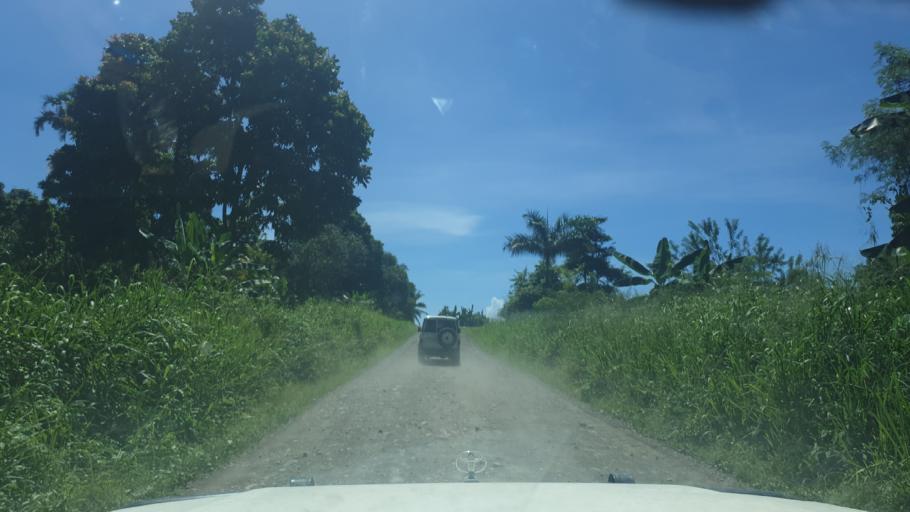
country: PG
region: Bougainville
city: Arawa
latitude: -5.8116
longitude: 155.1491
